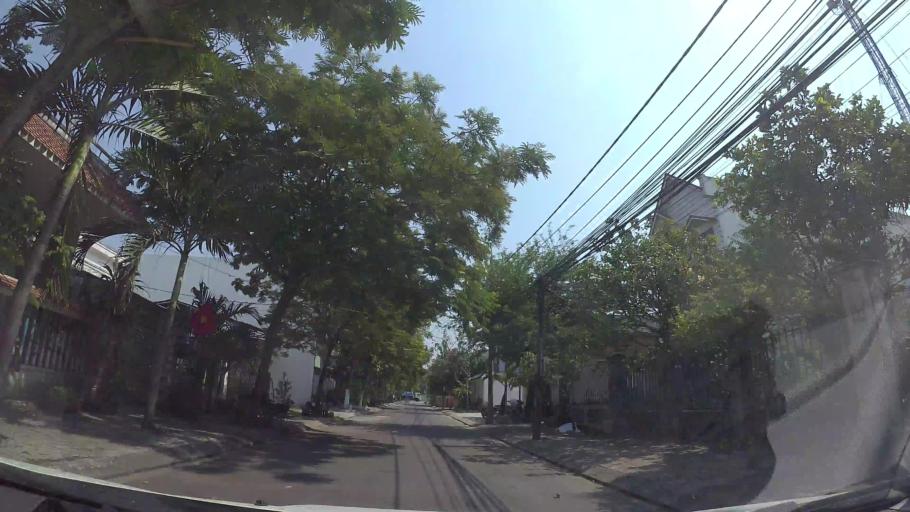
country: VN
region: Da Nang
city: Ngu Hanh Son
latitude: 15.9816
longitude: 108.2748
